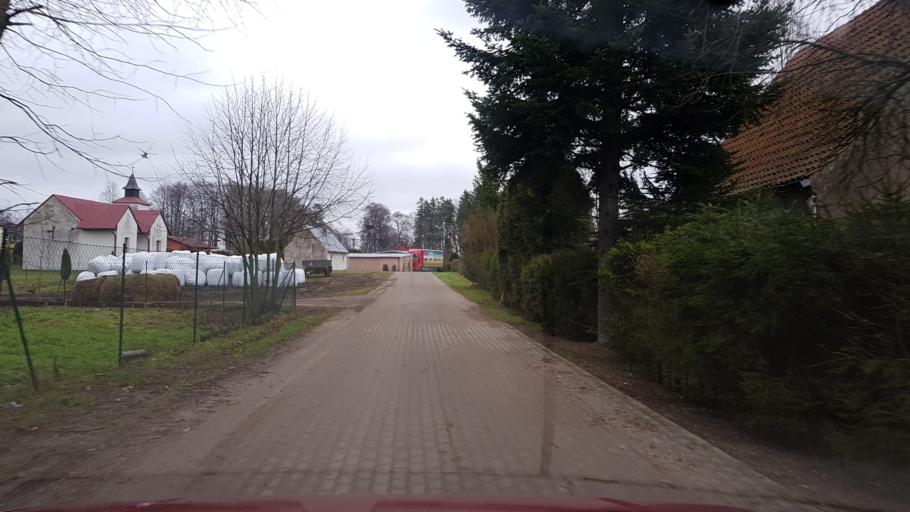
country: PL
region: Pomeranian Voivodeship
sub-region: Powiat bytowski
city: Tuchomie
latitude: 54.1464
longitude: 17.3177
